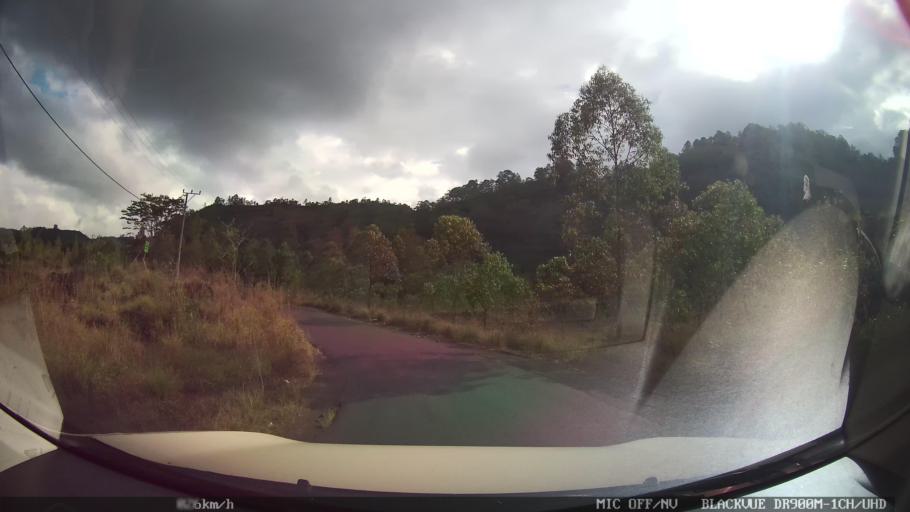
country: ID
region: Bali
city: Banjar Kedisan
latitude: -8.2449
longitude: 115.3490
